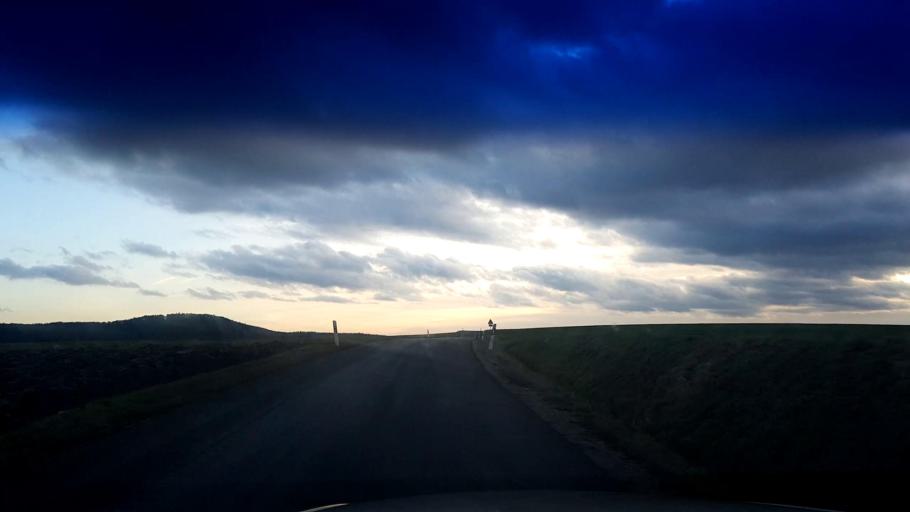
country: DE
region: Bavaria
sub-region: Upper Franconia
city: Buttenheim
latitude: 49.8188
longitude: 11.0543
